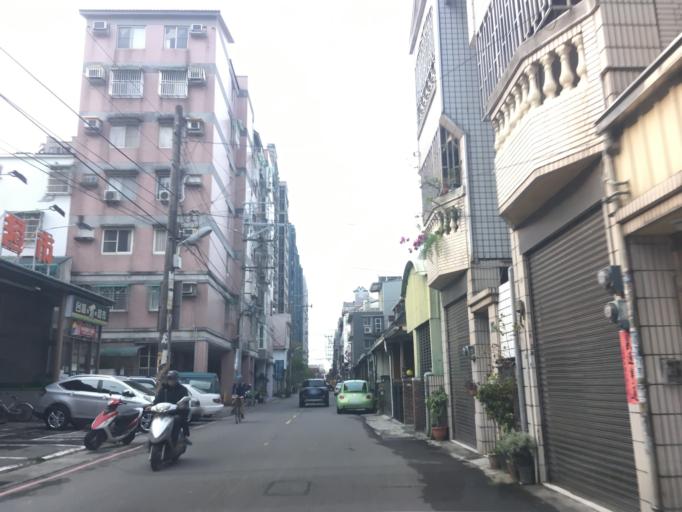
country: TW
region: Taiwan
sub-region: Taichung City
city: Taichung
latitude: 24.1919
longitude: 120.7018
